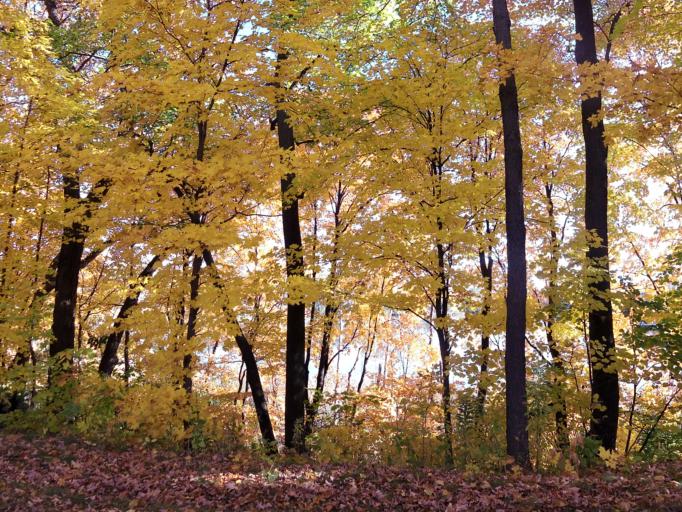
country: US
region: Minnesota
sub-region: Scott County
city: Prior Lake
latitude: 44.7026
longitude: -93.4365
